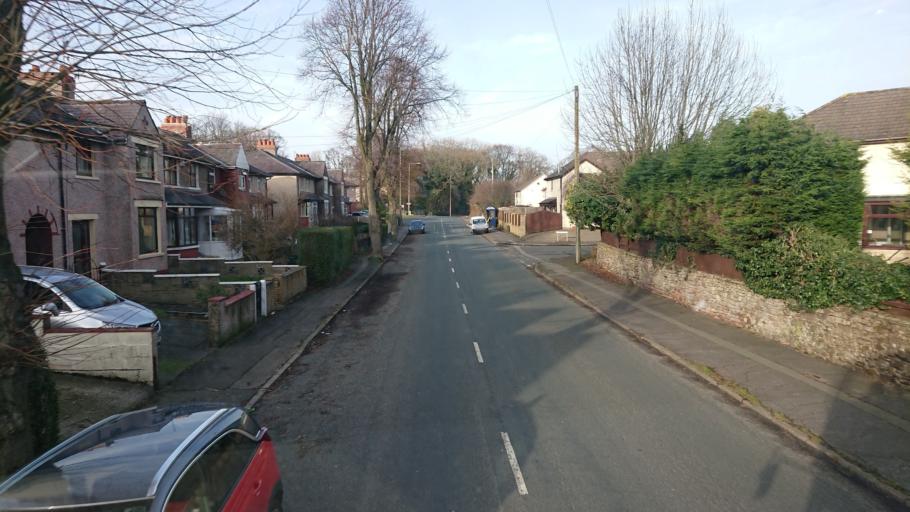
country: GB
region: England
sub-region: Lancashire
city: Lancaster
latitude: 54.0657
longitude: -2.7948
